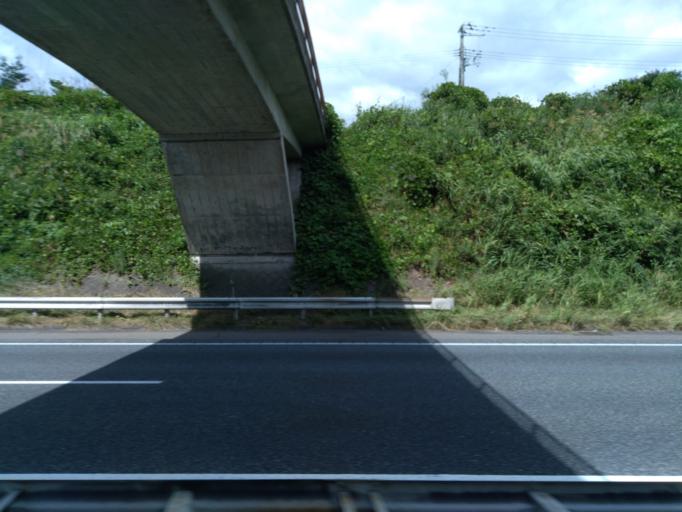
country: JP
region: Miyagi
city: Furukawa
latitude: 38.5029
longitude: 140.9298
